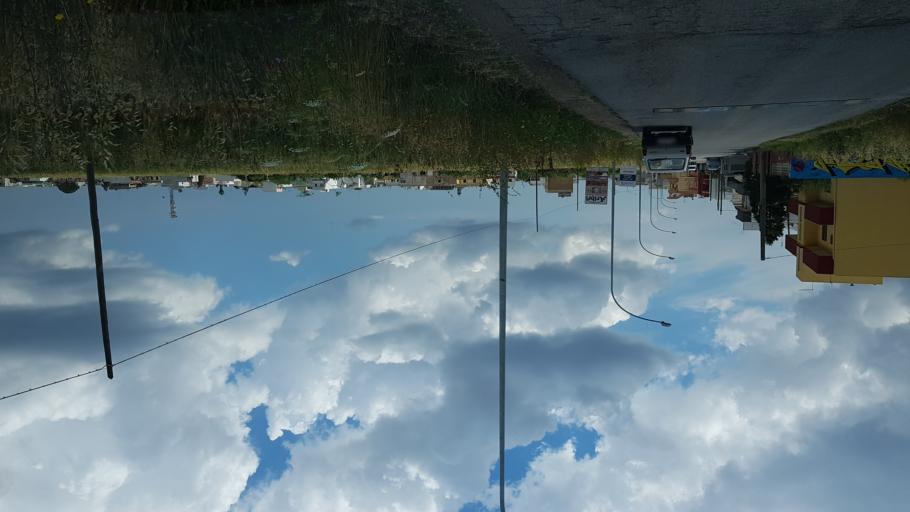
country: IT
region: Apulia
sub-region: Provincia di Brindisi
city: San Pancrazio Salentino
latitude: 40.4258
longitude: 17.8409
